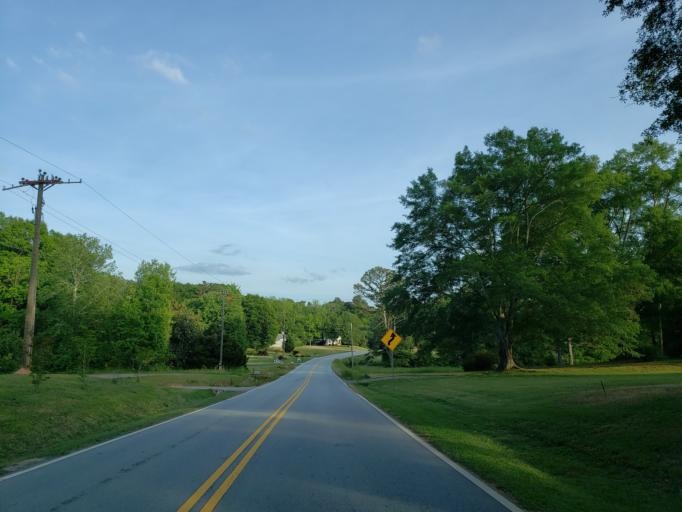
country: US
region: Georgia
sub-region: Carroll County
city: Mount Zion
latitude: 33.6037
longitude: -85.1421
